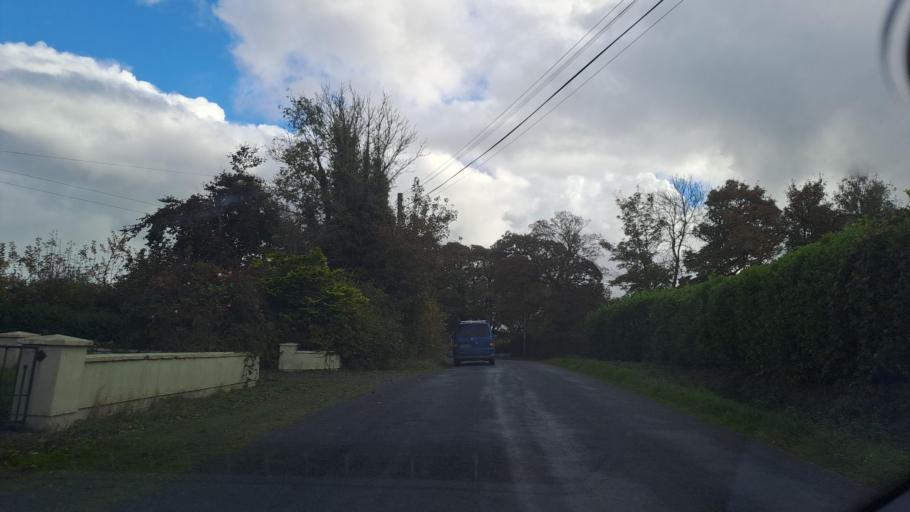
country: IE
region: Ulster
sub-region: An Cabhan
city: Bailieborough
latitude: 53.9924
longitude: -6.9279
